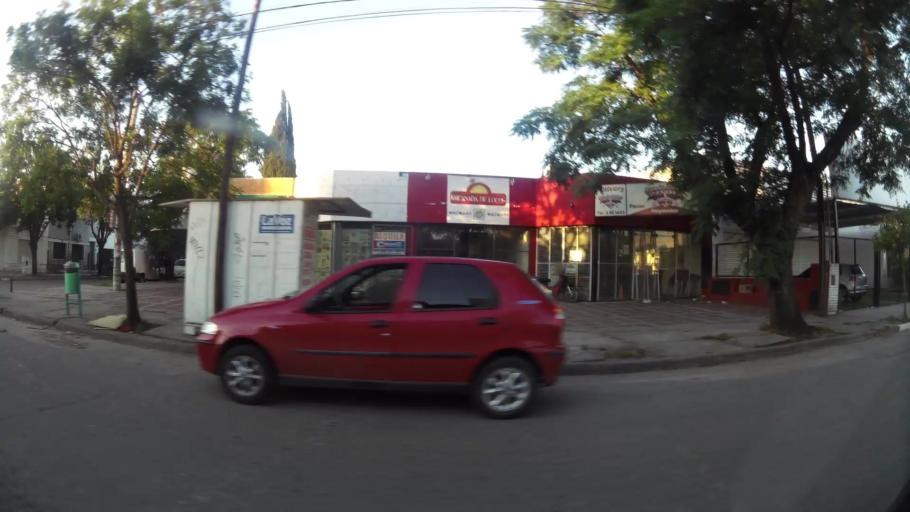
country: AR
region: Cordoba
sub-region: Departamento de Capital
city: Cordoba
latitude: -31.3737
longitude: -64.2167
